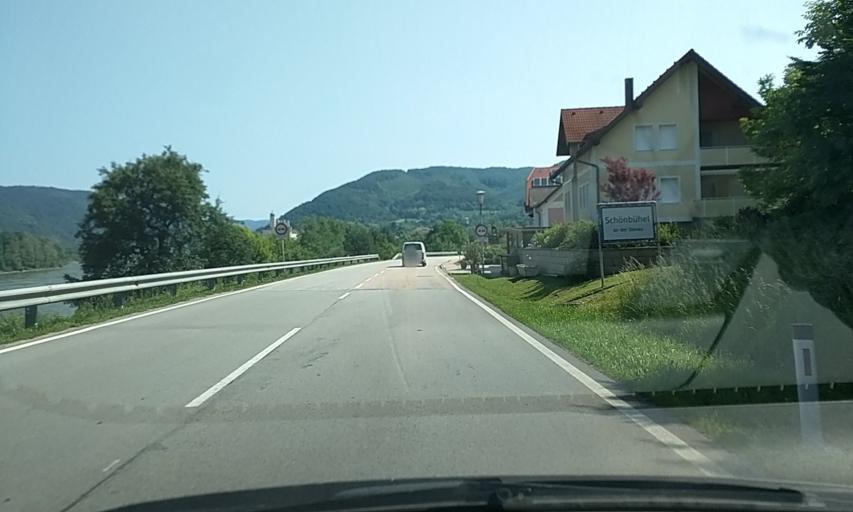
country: AT
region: Lower Austria
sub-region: Politischer Bezirk Melk
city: Emmersdorf an der Donau
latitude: 48.2505
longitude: 15.3654
